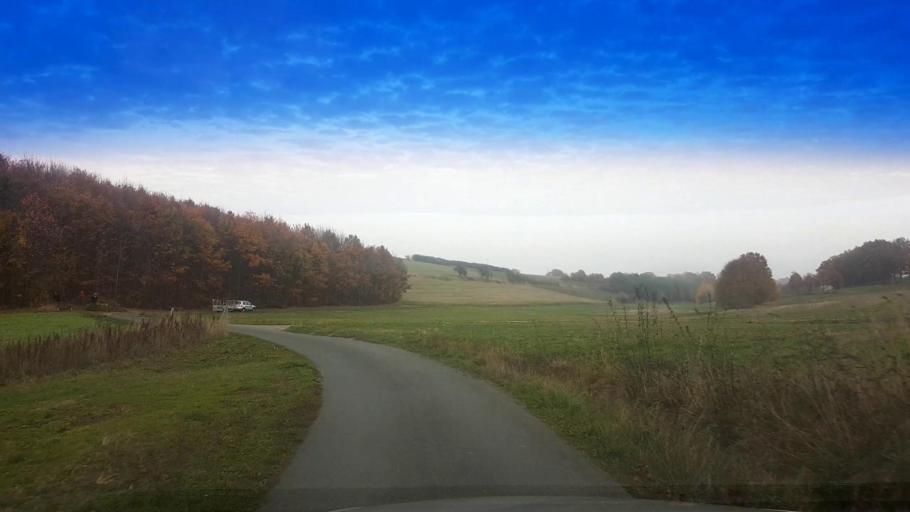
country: DE
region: Bavaria
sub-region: Upper Franconia
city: Viereth-Trunstadt
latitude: 49.9212
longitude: 10.7478
